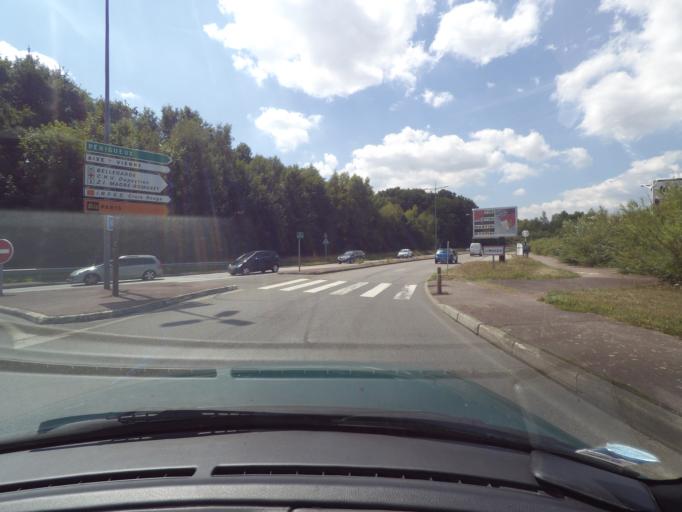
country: FR
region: Limousin
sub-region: Departement de la Haute-Vienne
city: Condat-sur-Vienne
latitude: 45.8038
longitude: 1.2916
